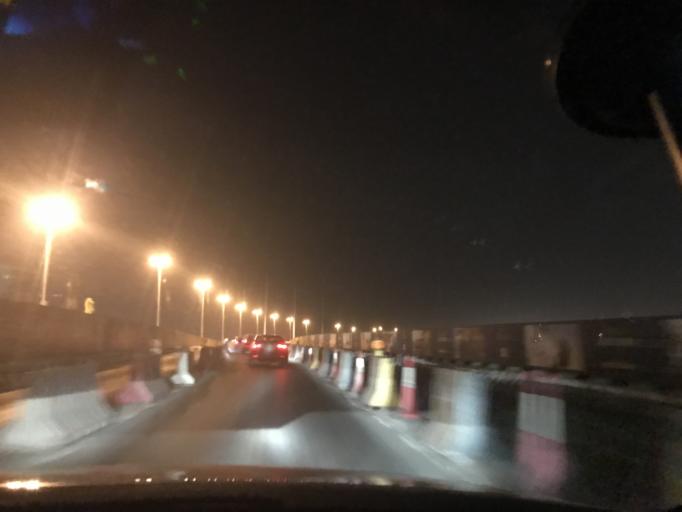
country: BH
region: Muharraq
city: Al Muharraq
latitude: 26.3033
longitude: 50.6407
